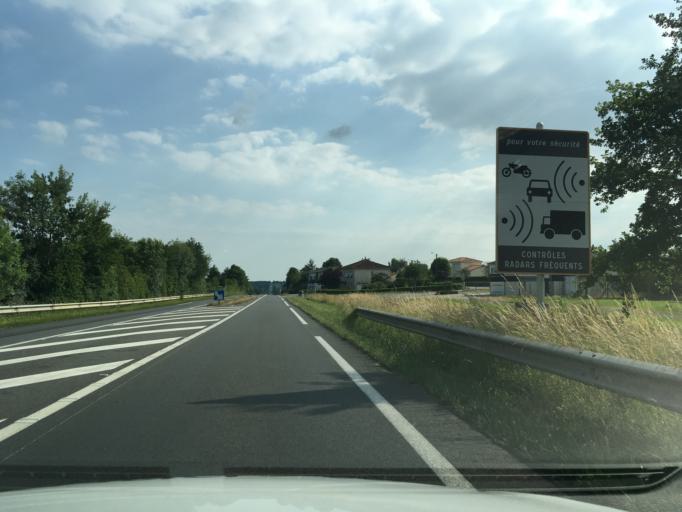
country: FR
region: Poitou-Charentes
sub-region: Departement des Deux-Sevres
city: Saint-Pardoux
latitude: 46.5733
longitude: -0.2958
